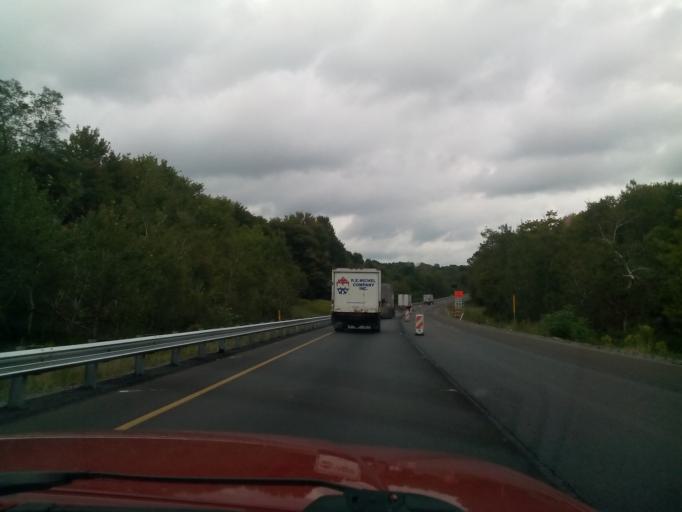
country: US
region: Pennsylvania
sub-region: Jefferson County
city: Falls Creek
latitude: 41.1573
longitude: -78.8317
